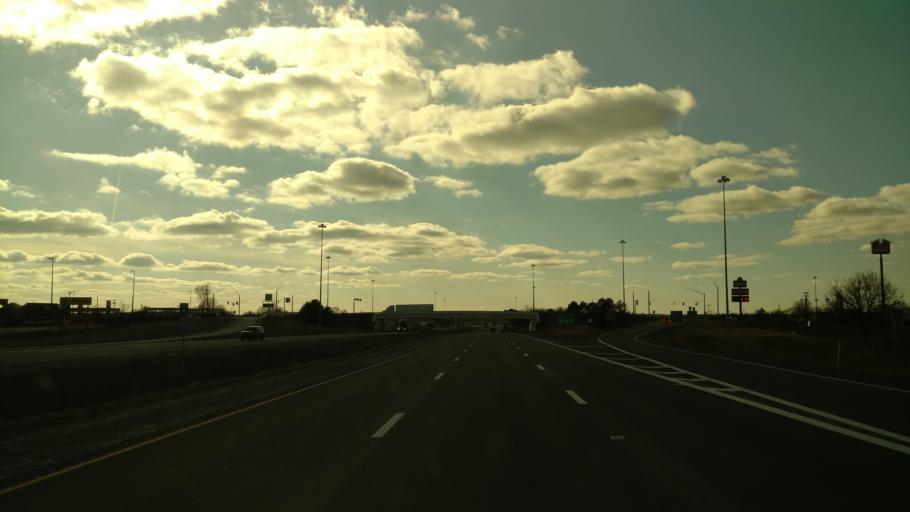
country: US
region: Ohio
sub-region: Medina County
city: Lodi
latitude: 40.9977
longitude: -81.9927
